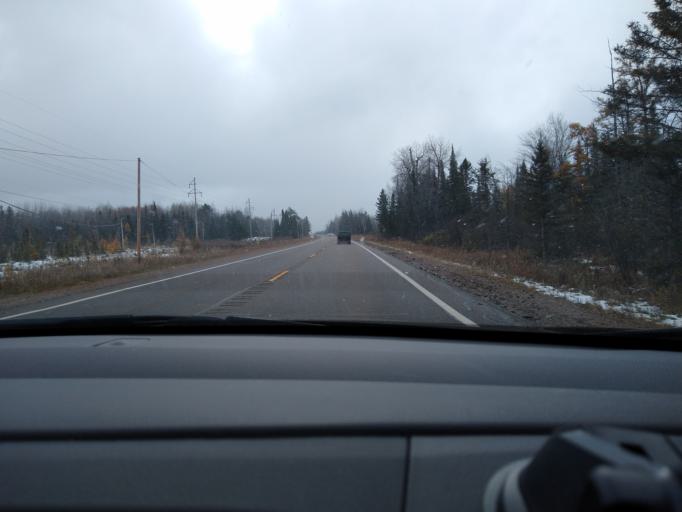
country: US
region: Michigan
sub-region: Dickinson County
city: Iron Mountain
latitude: 46.0263
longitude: -88.0606
